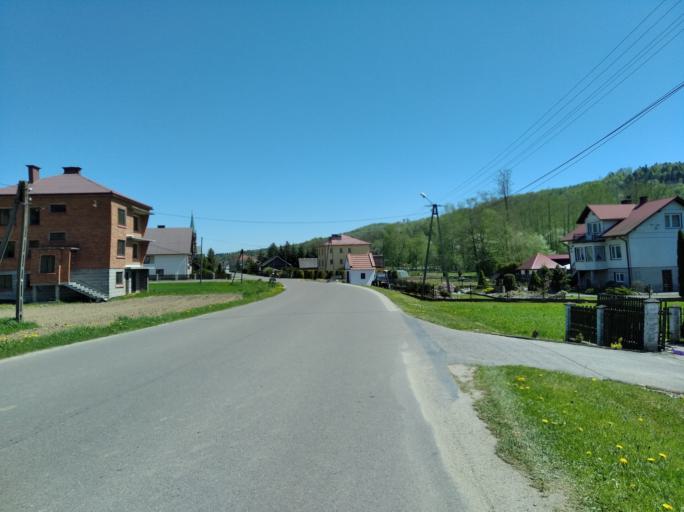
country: PL
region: Subcarpathian Voivodeship
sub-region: Powiat debicki
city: Brzostek
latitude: 49.9150
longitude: 21.4110
